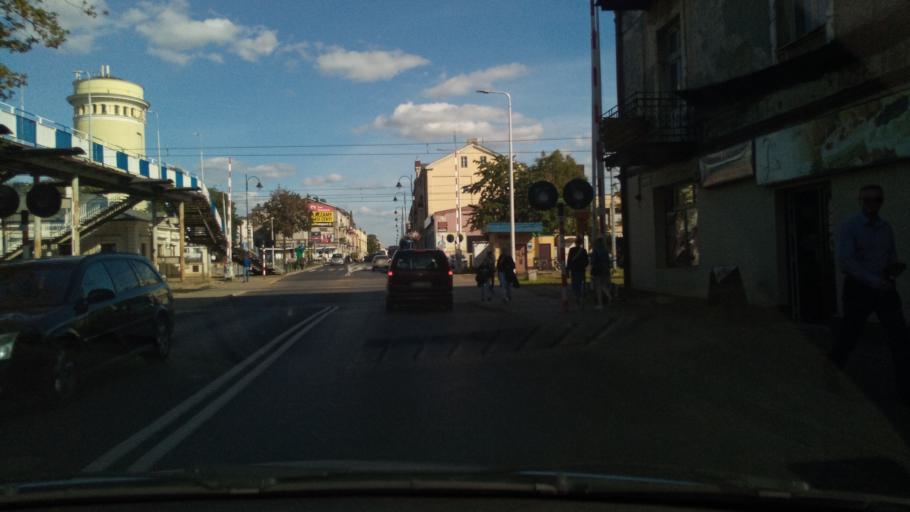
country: PL
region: Lodz Voivodeship
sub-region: Piotrkow Trybunalski
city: Piotrkow Trybunalski
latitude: 51.4092
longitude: 19.6839
